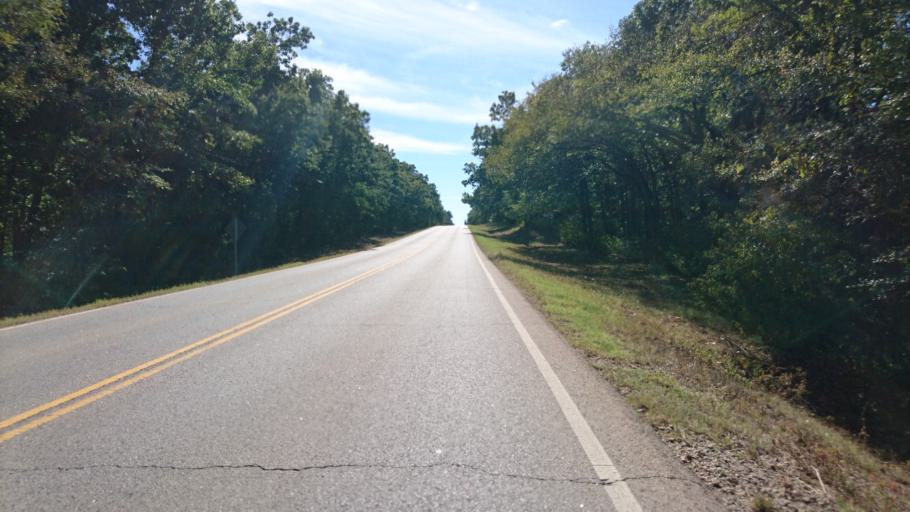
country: US
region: Oklahoma
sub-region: Lincoln County
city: Stroud
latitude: 35.7334
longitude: -96.7229
